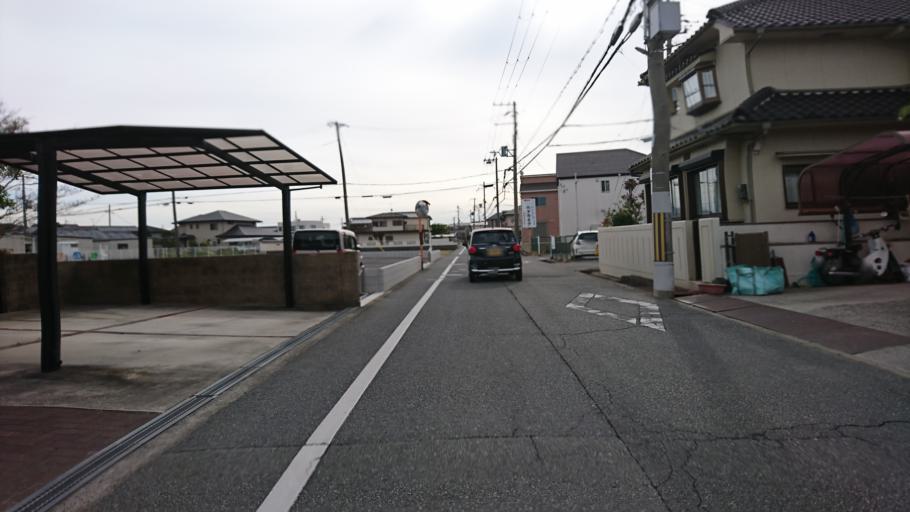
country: JP
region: Hyogo
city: Kakogawacho-honmachi
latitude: 34.7751
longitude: 134.8561
